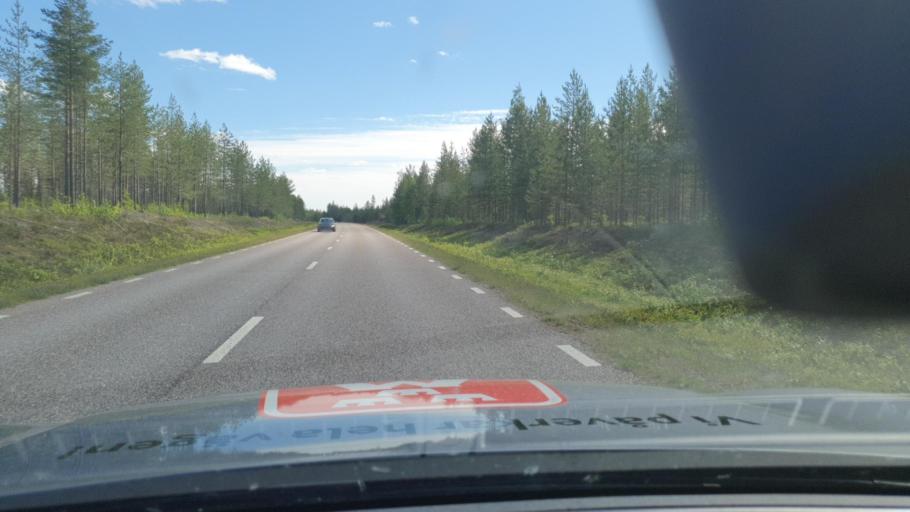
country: FI
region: Lapland
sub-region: Tunturi-Lappi
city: Kolari
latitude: 67.0427
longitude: 23.6896
